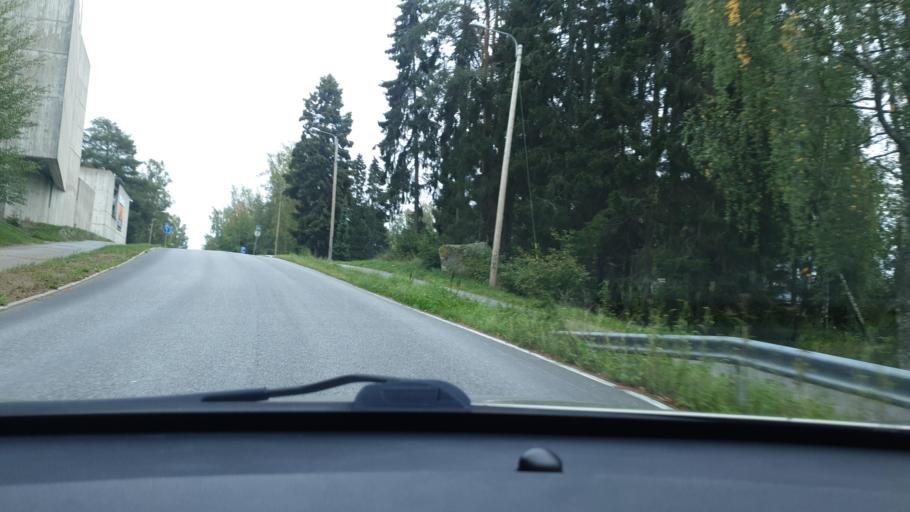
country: FI
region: Ostrobothnia
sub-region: Vaasa
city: Korsholm
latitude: 63.0965
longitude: 21.6622
